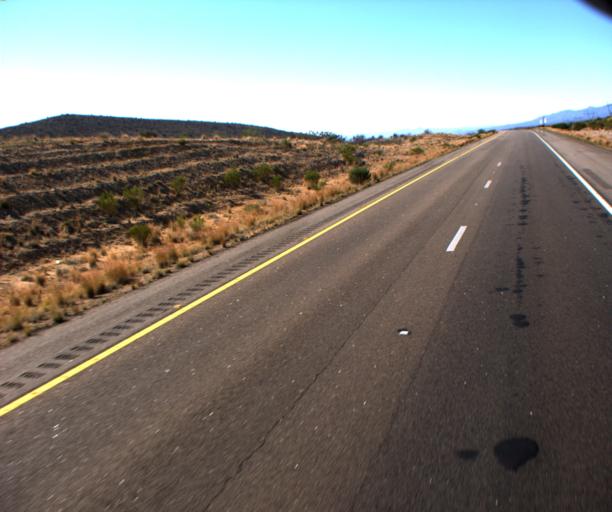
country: US
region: Arizona
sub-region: Mohave County
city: Kingman
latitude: 34.9556
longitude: -113.6695
